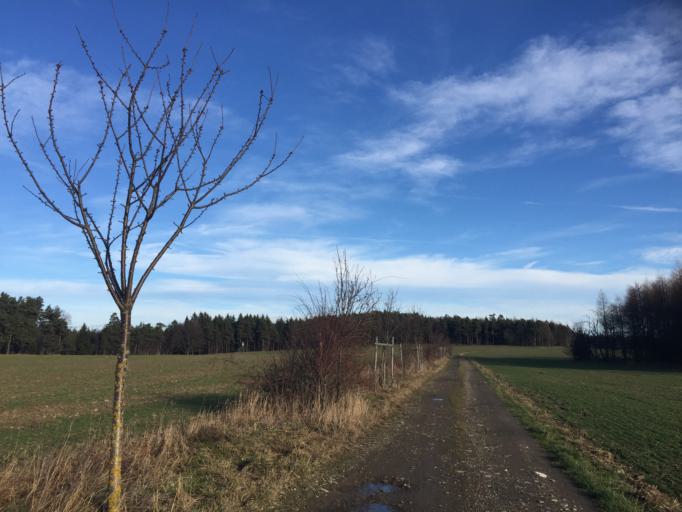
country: DE
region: Thuringia
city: Doschnitz
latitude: 50.6394
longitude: 11.2635
